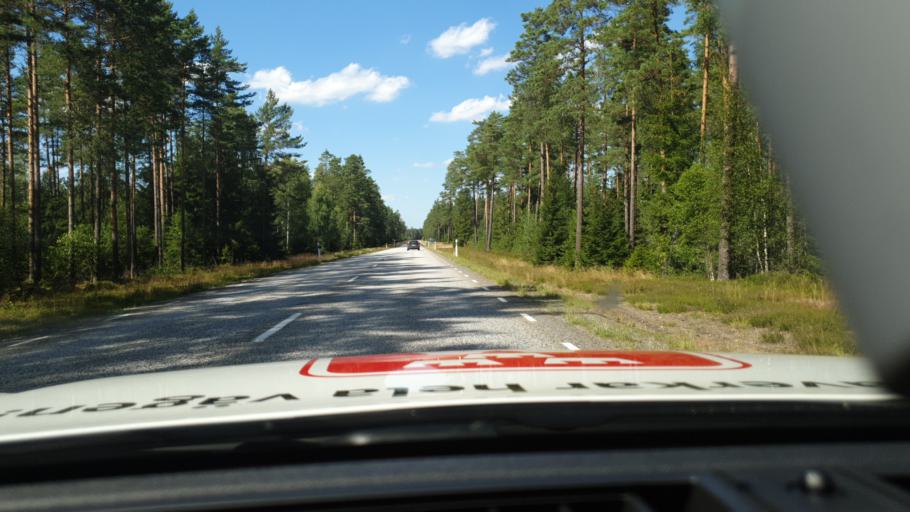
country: SE
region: Joenkoeping
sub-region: Vaggeryds Kommun
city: Vaggeryd
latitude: 57.5817
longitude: 14.2298
